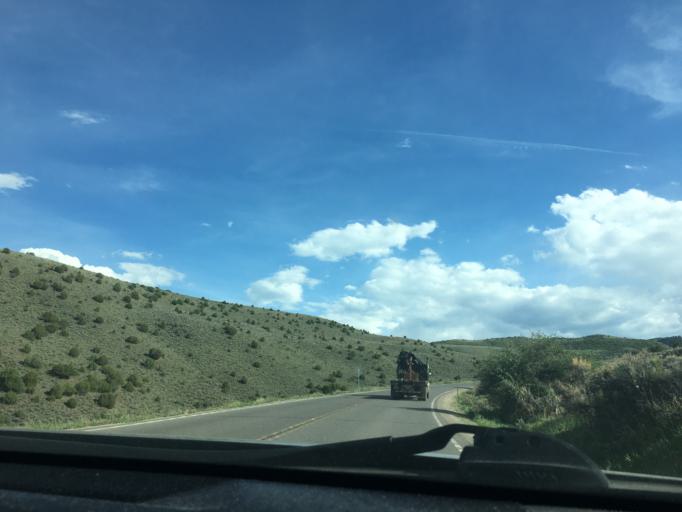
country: US
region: Colorado
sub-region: Eagle County
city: Edwards
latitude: 39.8326
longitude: -106.6382
